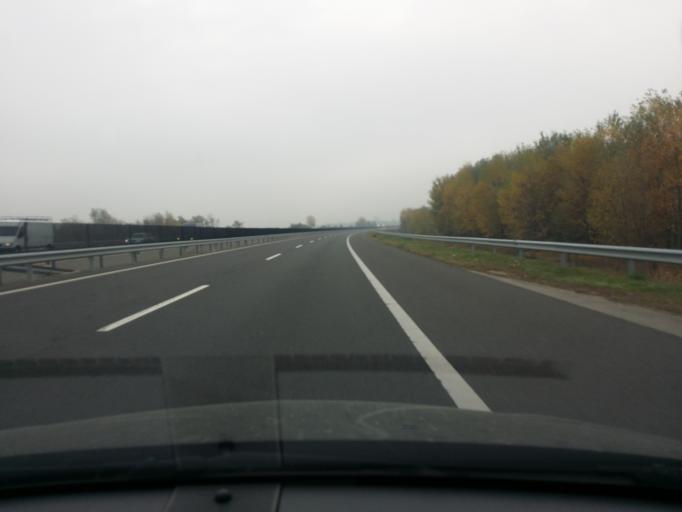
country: HU
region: Szabolcs-Szatmar-Bereg
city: Kalmanhaza
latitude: 47.9032
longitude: 21.5856
